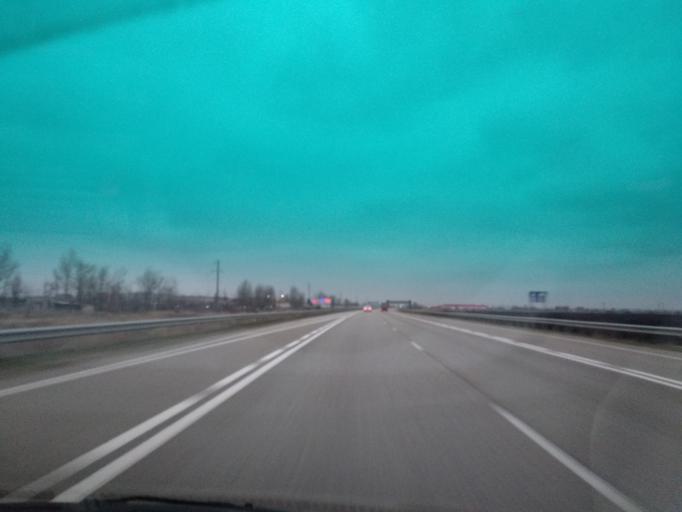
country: RU
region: Adygeya
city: Adygeysk
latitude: 44.8872
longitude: 39.1722
